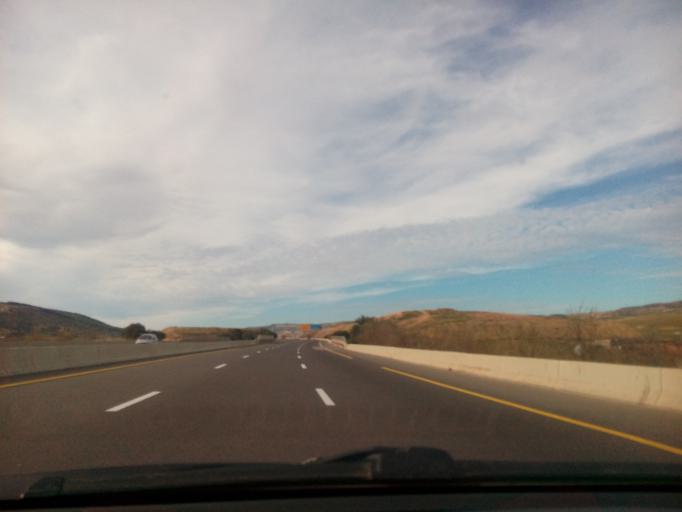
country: DZ
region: Sidi Bel Abbes
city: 'Ain el Berd
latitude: 35.4454
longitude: -0.4054
